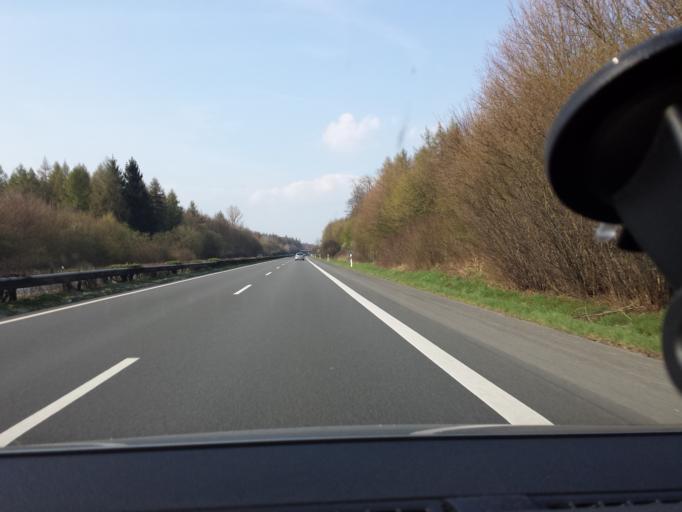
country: DE
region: Lower Saxony
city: Flothe
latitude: 52.1013
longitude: 10.4913
